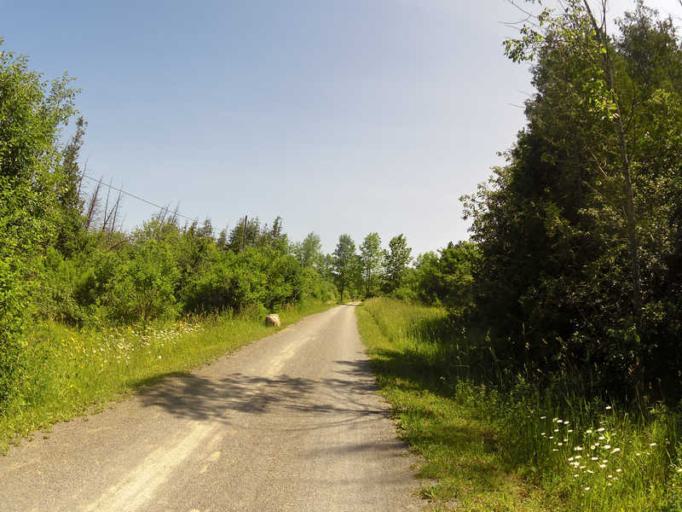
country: CA
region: Ontario
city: Peterborough
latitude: 44.3742
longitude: -78.2843
